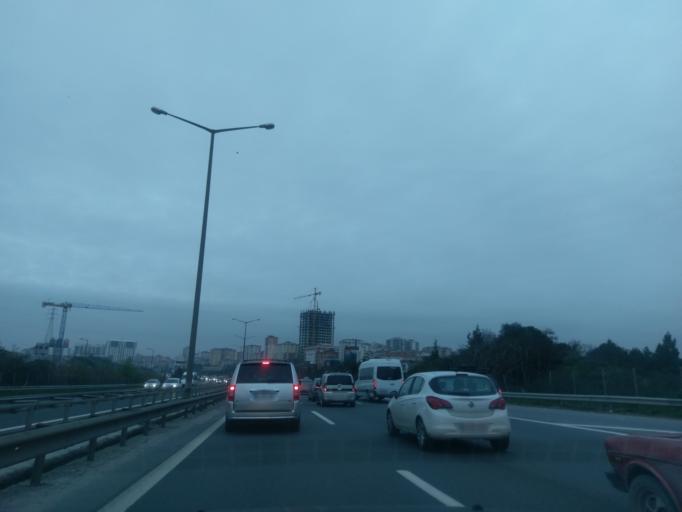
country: TR
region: Istanbul
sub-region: Atasehir
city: Atasehir
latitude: 40.9974
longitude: 29.1175
